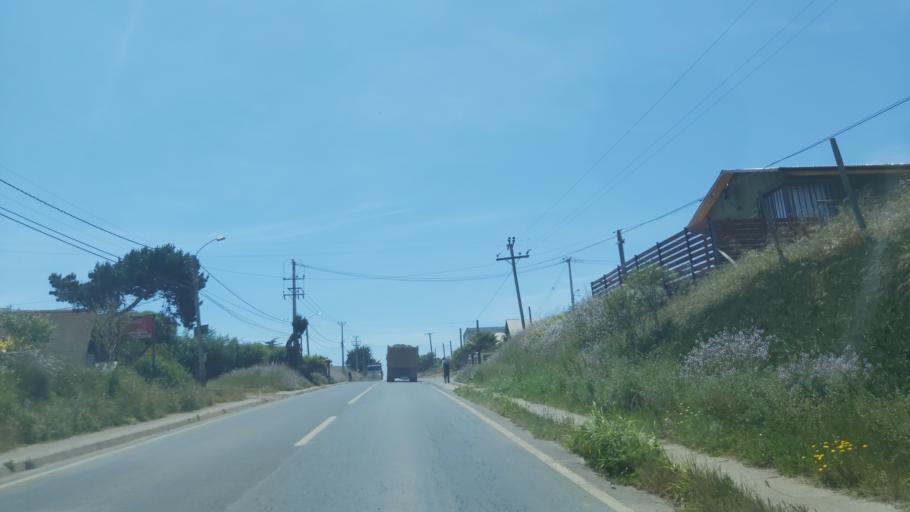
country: CL
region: Maule
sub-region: Provincia de Cauquenes
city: Cauquenes
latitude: -35.8040
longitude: -72.5668
